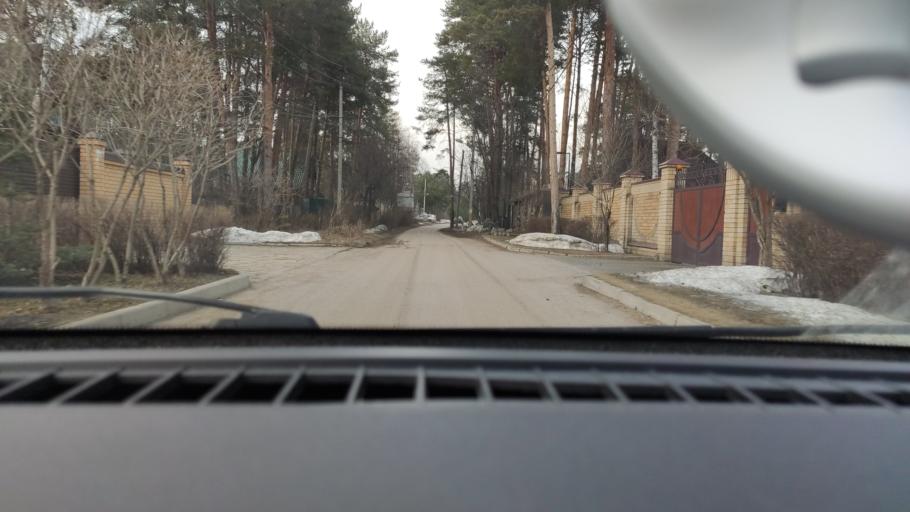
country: RU
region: Perm
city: Perm
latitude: 58.0537
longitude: 56.2998
